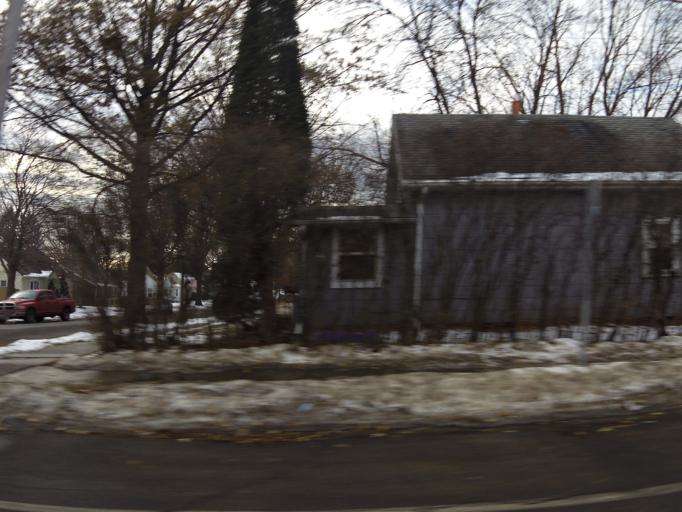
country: US
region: Minnesota
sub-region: Ramsey County
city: Maplewood
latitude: 44.9588
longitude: -93.0152
